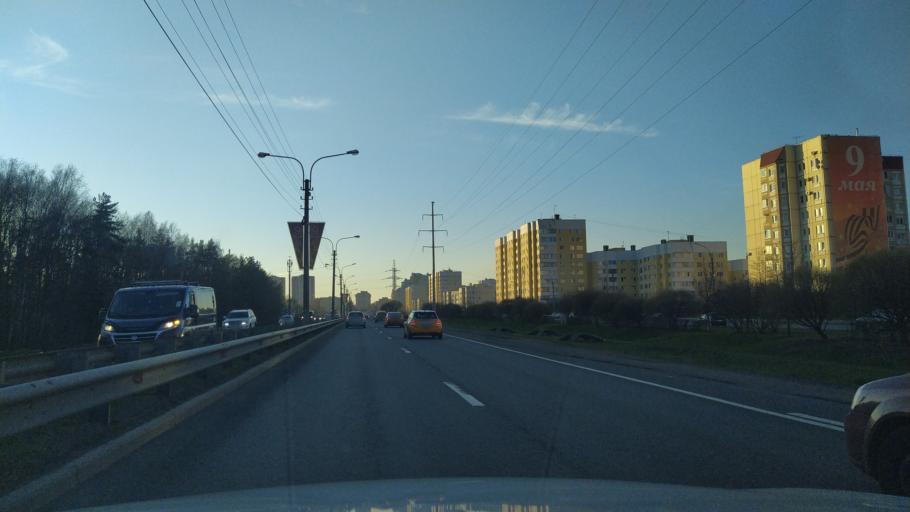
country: RU
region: St.-Petersburg
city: Razliv
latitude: 60.0768
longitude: 29.9638
